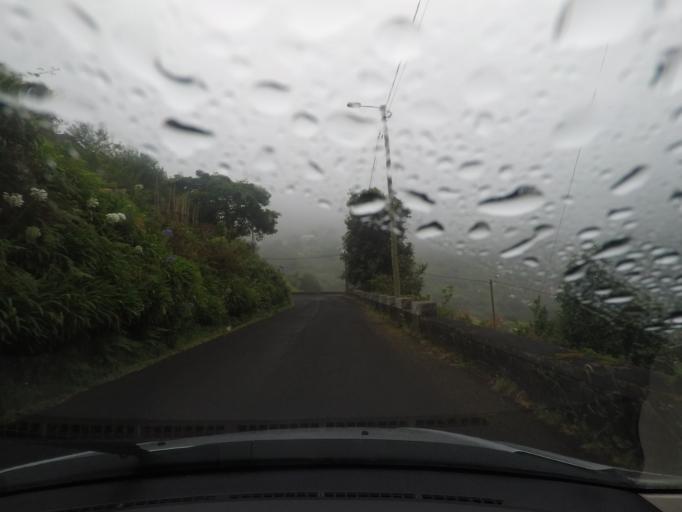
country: PT
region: Madeira
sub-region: Santana
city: Santana
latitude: 32.7536
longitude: -16.8773
